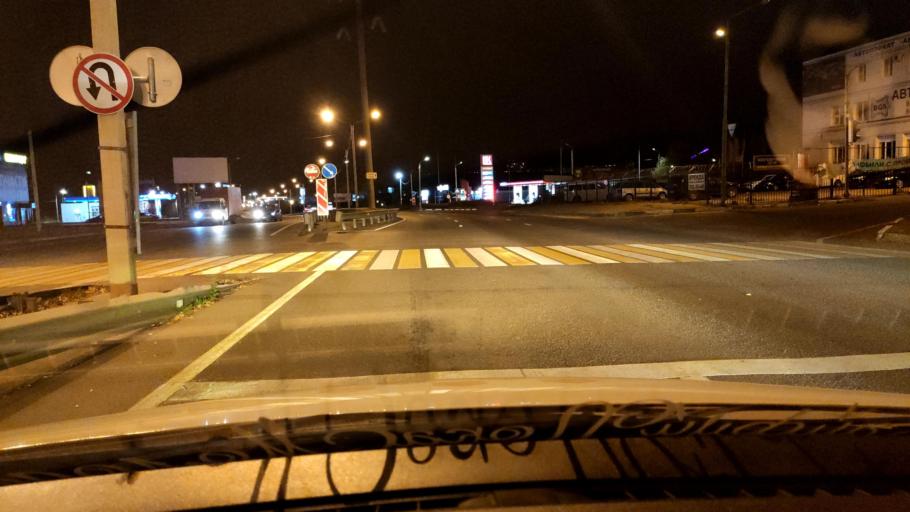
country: RU
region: Voronezj
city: Pridonskoy
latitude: 51.6663
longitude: 39.1272
